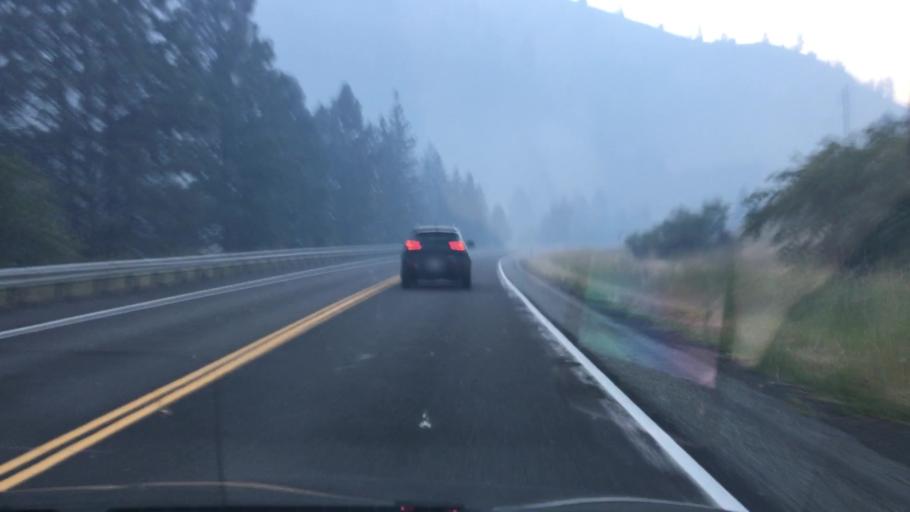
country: US
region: Idaho
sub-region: Valley County
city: McCall
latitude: 45.2696
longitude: -116.3446
